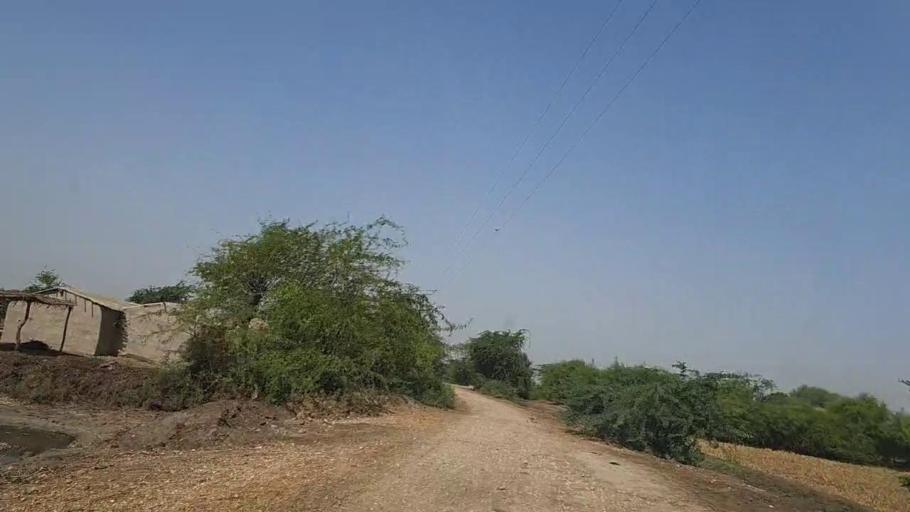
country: PK
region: Sindh
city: Daro Mehar
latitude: 24.7476
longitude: 68.1402
